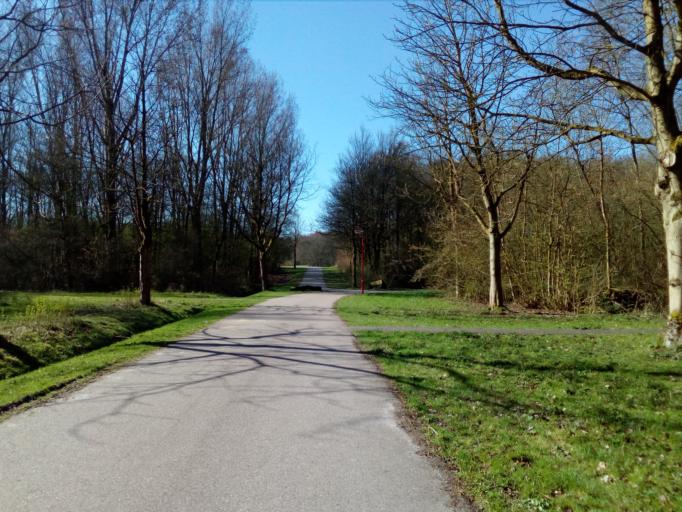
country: NL
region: South Holland
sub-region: Gemeente Zoetermeer
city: Zoetermeer
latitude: 52.0534
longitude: 4.4539
